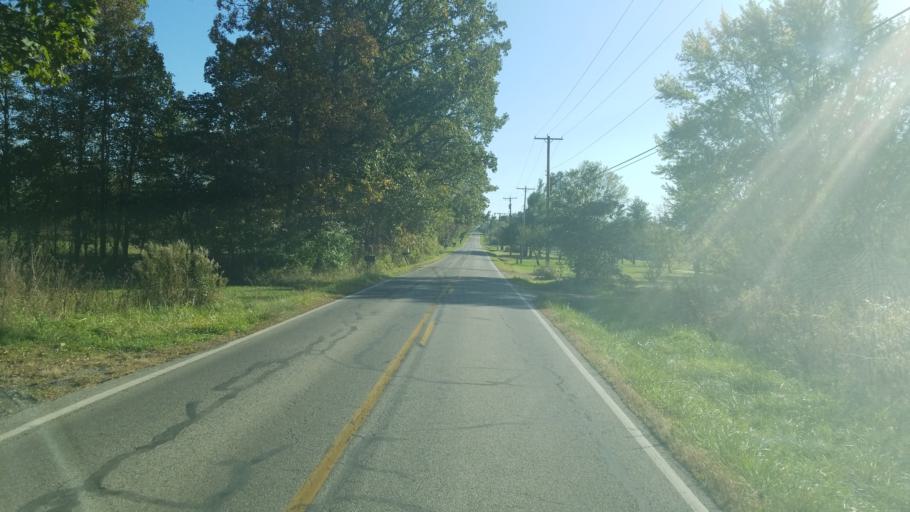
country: US
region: Ohio
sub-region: Medina County
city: Westfield Center
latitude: 41.0176
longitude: -81.9108
